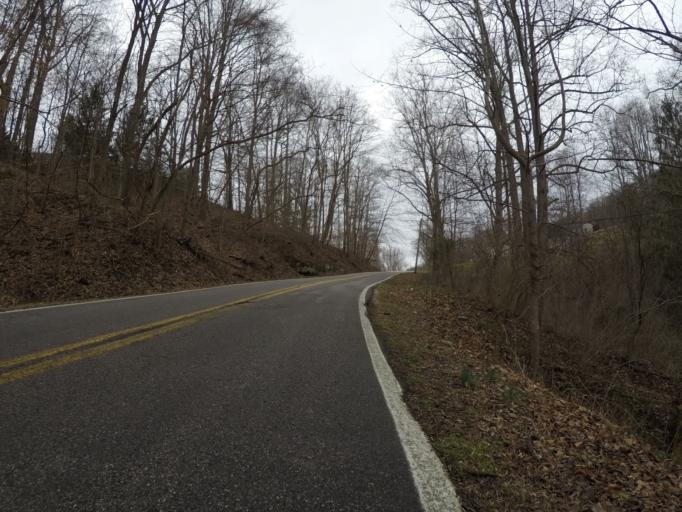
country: US
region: West Virginia
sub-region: Cabell County
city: Barboursville
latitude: 38.4548
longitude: -82.2652
